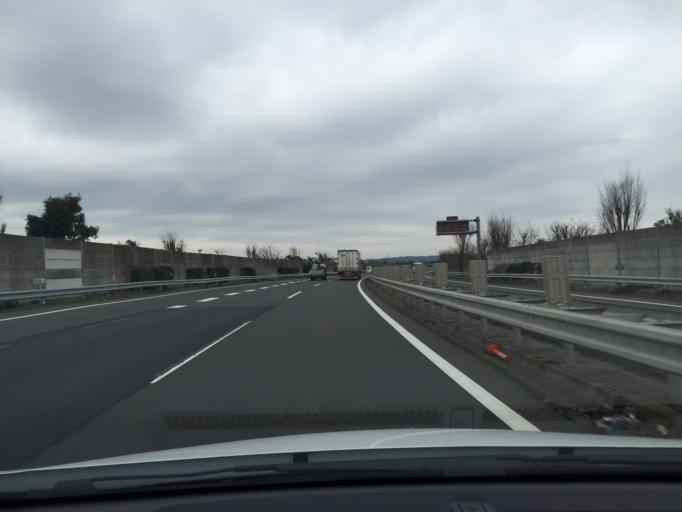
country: JP
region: Saitama
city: Sayama
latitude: 35.8632
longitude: 139.3778
